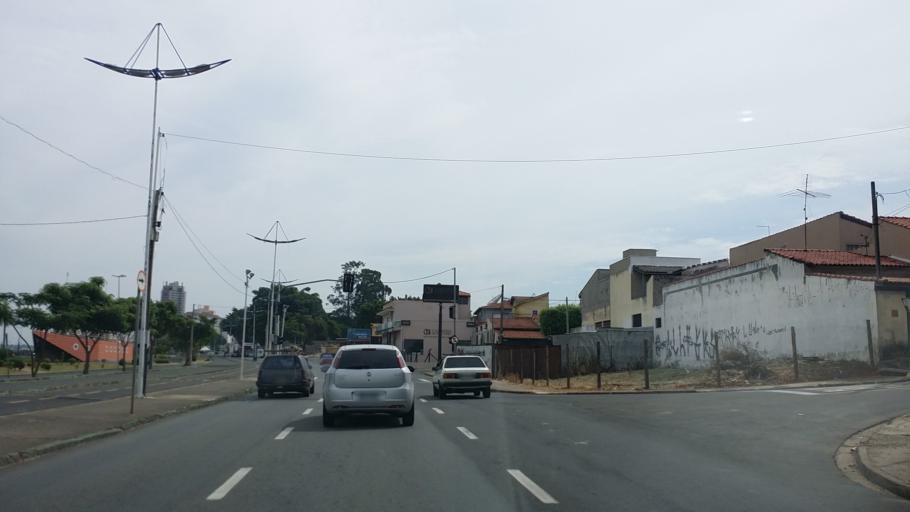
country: BR
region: Sao Paulo
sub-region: Indaiatuba
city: Indaiatuba
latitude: -23.1050
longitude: -47.2276
